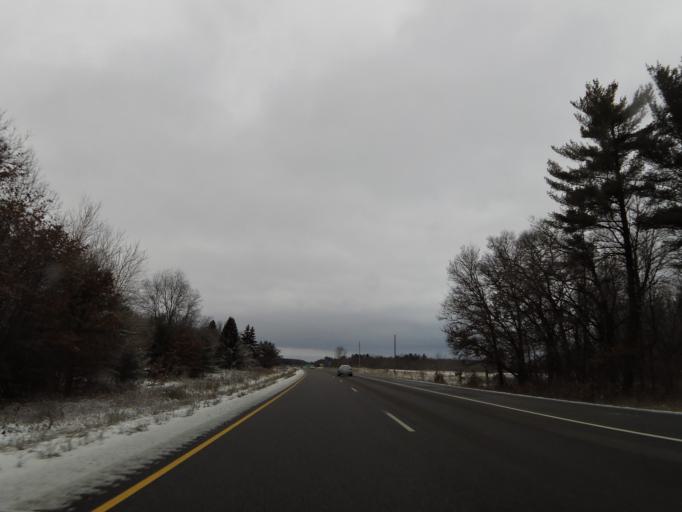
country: US
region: Wisconsin
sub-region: Eau Claire County
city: Altoona
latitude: 44.7510
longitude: -91.3861
